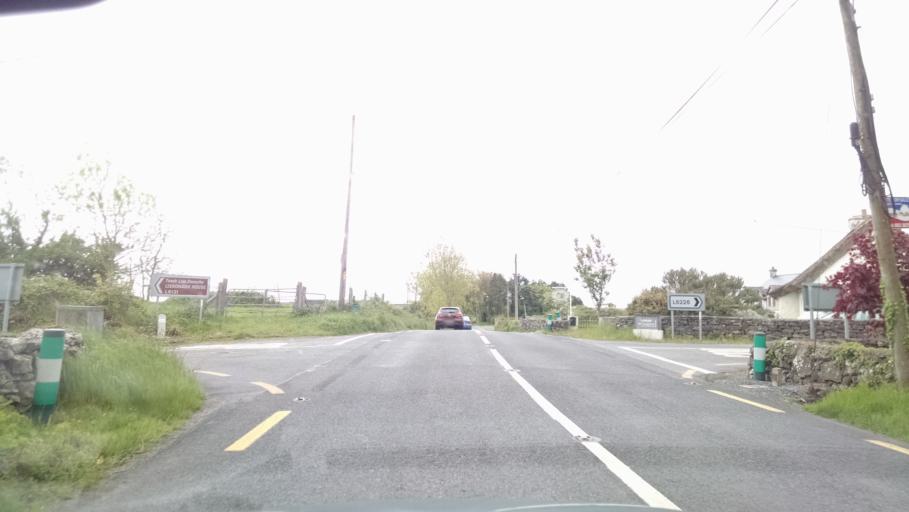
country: IE
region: Connaught
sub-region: County Galway
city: Moycullen
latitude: 53.4992
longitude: -9.0797
